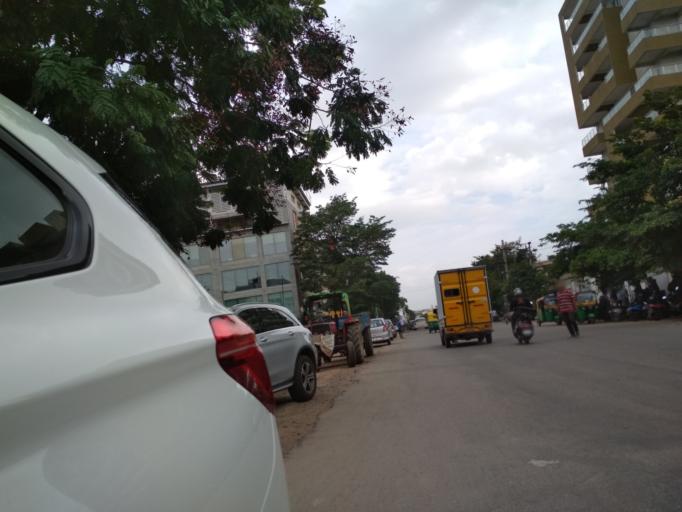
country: IN
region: Karnataka
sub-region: Bangalore Urban
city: Bangalore
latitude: 12.9195
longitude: 77.6450
